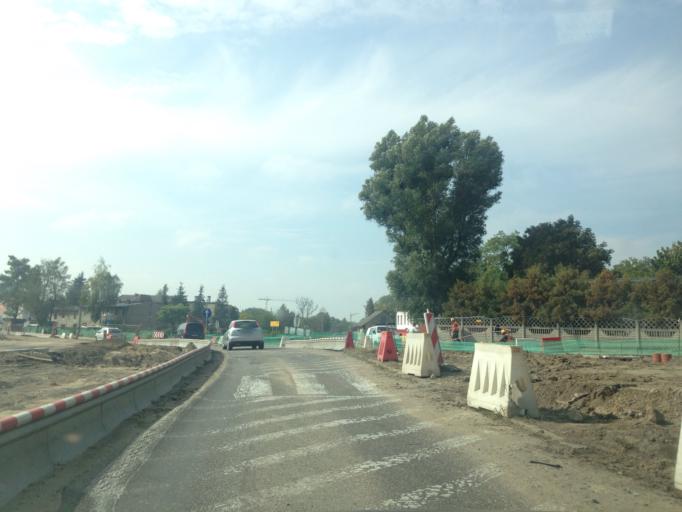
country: PL
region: Kujawsko-Pomorskie
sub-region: Powiat brodnicki
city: Brodnica
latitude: 53.2656
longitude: 19.4061
